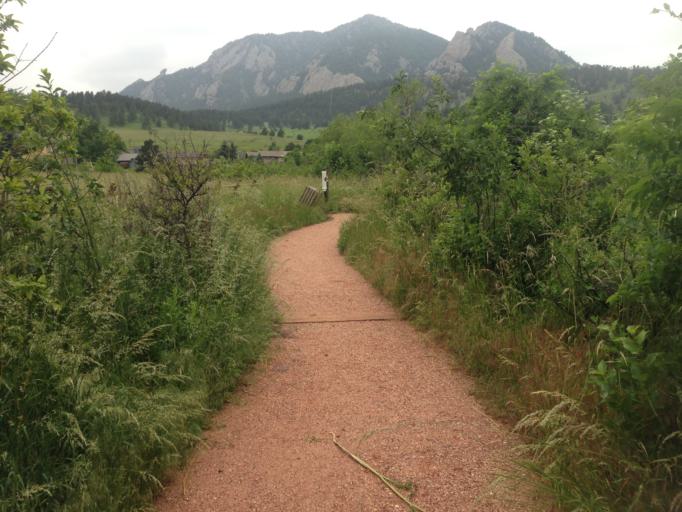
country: US
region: Colorado
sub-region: Boulder County
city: Boulder
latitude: 39.9745
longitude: -105.2671
